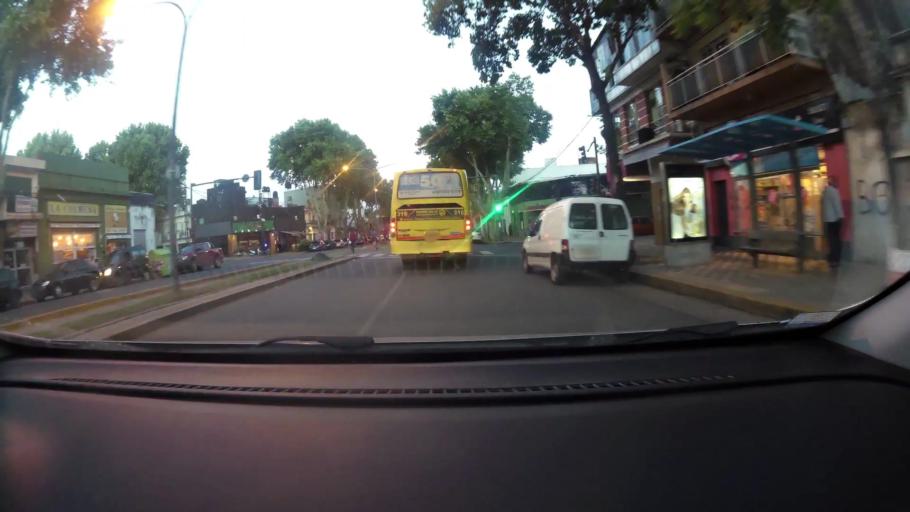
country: AR
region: Santa Fe
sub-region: Departamento de Rosario
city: Rosario
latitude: -32.9567
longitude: -60.6752
